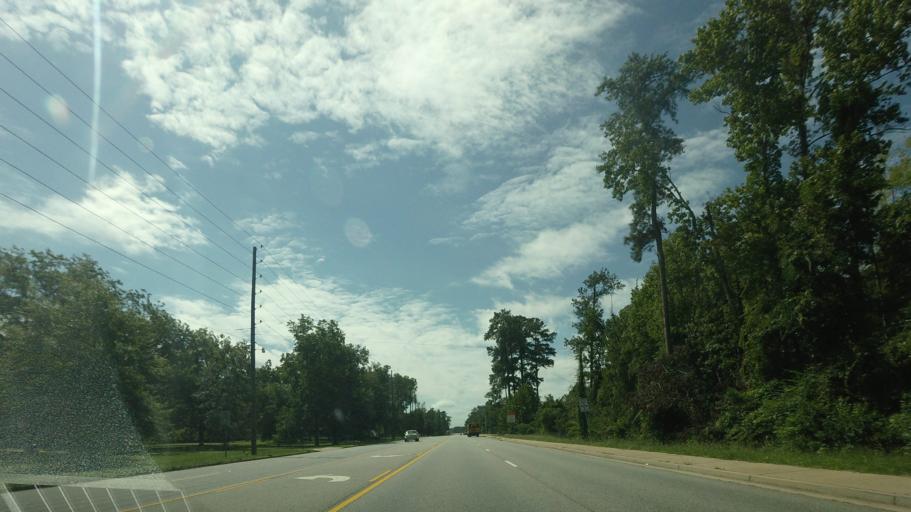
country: US
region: Georgia
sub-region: Houston County
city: Centerville
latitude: 32.5592
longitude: -83.6912
